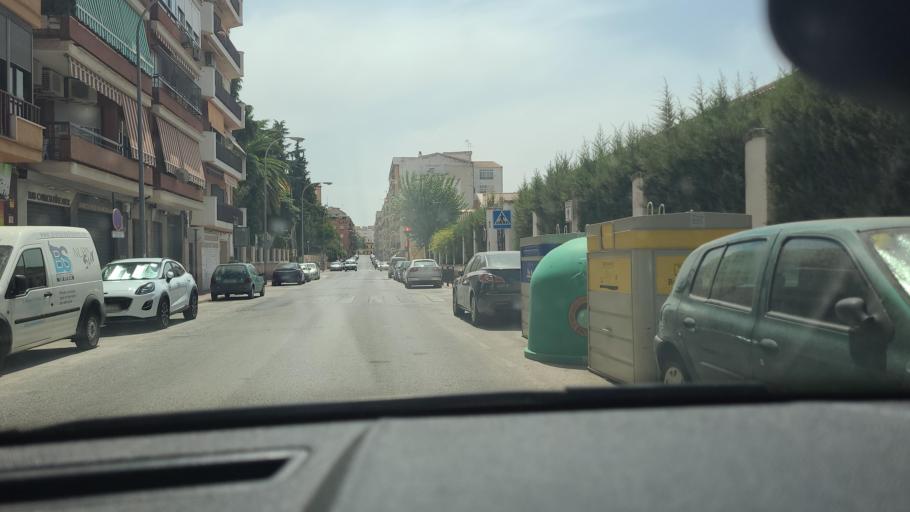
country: ES
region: Andalusia
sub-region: Provincia de Jaen
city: Linares
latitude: 38.0936
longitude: -3.6283
